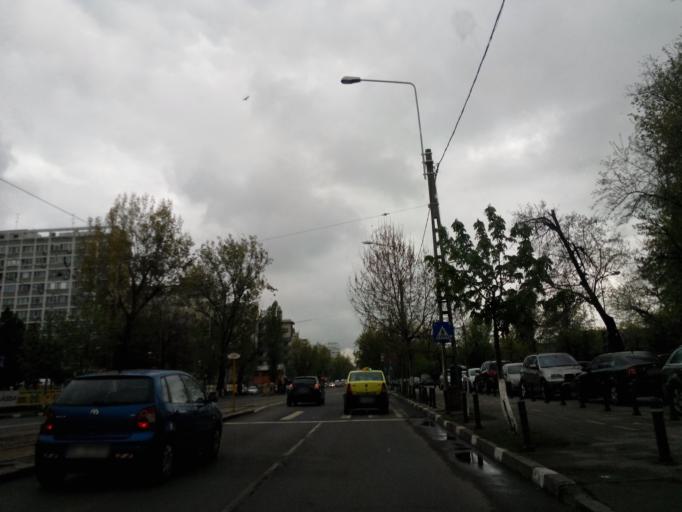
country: RO
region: Ilfov
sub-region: Comuna Fundeni-Dobroesti
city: Fundeni
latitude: 44.4332
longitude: 26.1495
